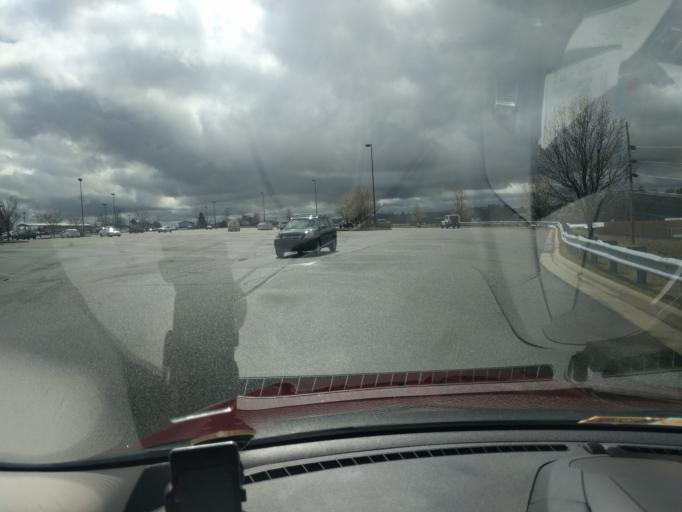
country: US
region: West Virginia
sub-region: Raleigh County
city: Stanaford
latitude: 37.8031
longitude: -81.1764
